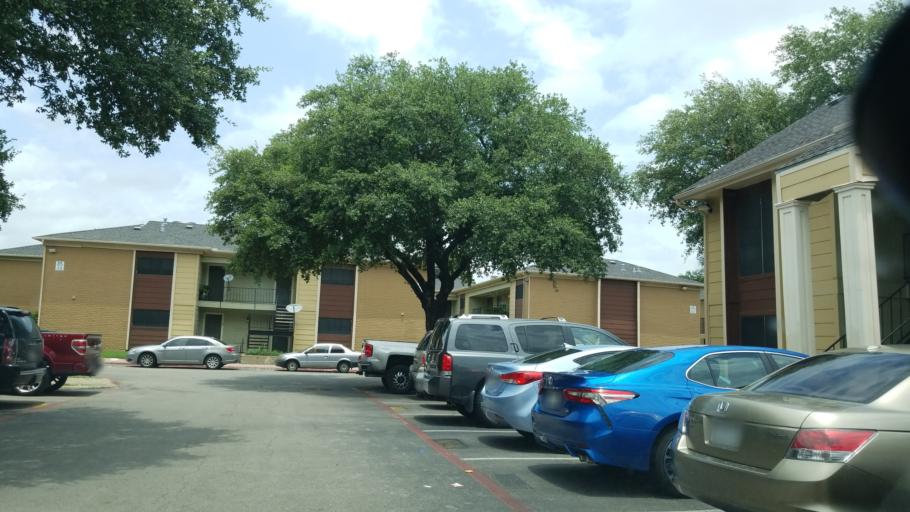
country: US
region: Texas
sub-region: Dallas County
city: Farmers Branch
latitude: 32.8719
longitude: -96.8694
